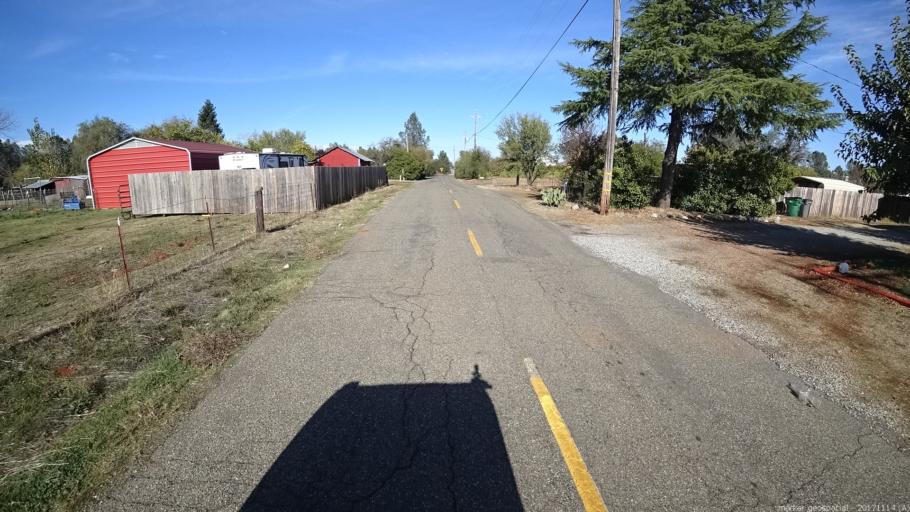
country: US
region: California
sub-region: Shasta County
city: Anderson
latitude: 40.4452
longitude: -122.4265
